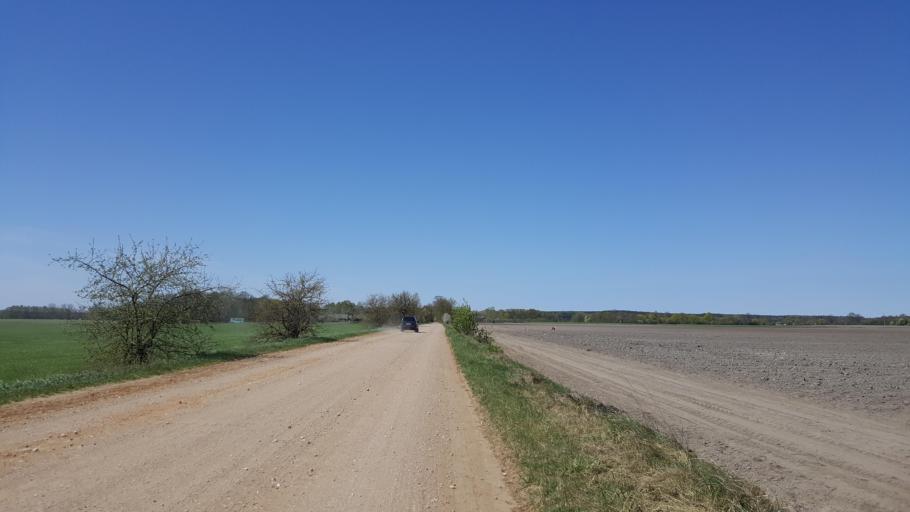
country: BY
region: Brest
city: Kamyanyets
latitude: 52.3285
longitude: 23.7669
